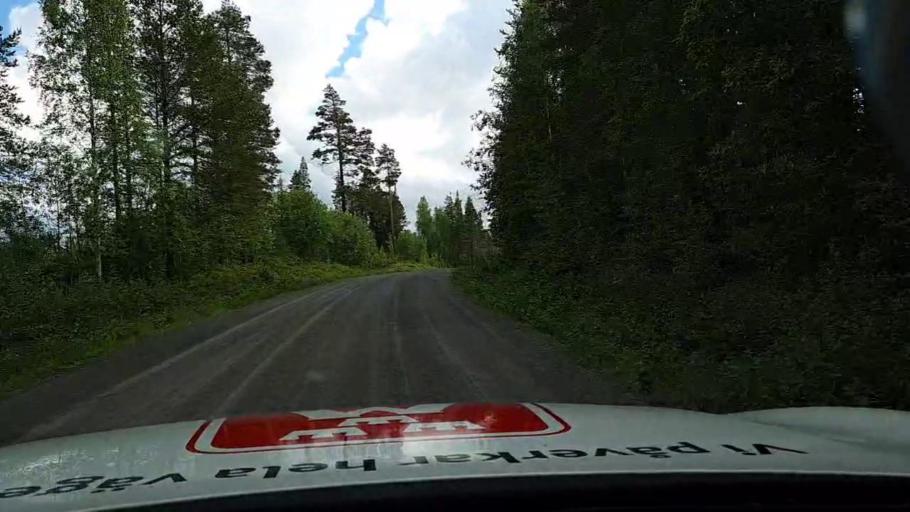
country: SE
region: Jaemtland
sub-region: OEstersunds Kommun
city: Brunflo
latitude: 63.1206
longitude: 15.0913
